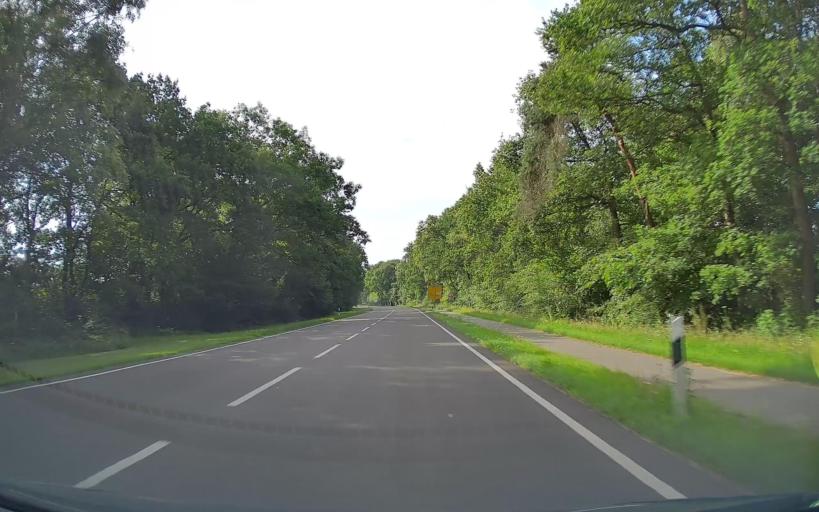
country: DE
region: Lower Saxony
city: Molbergen
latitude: 52.9208
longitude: 7.9536
